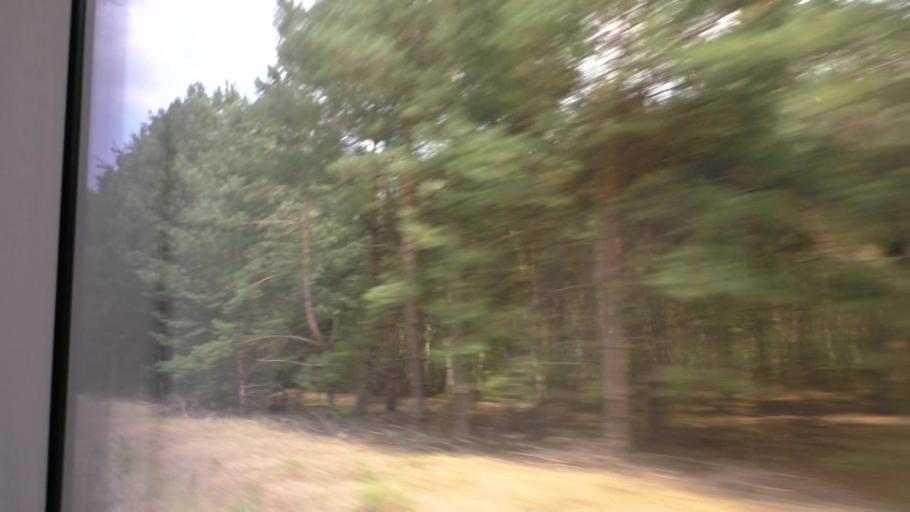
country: DE
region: Brandenburg
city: Mixdorf
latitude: 52.1788
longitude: 14.3832
